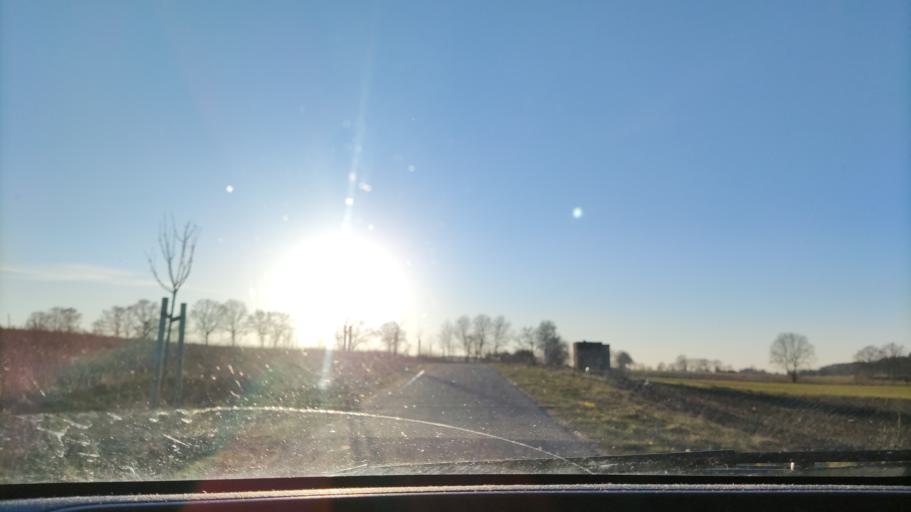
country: DE
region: Lower Saxony
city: Gohrde
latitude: 53.1609
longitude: 10.8584
